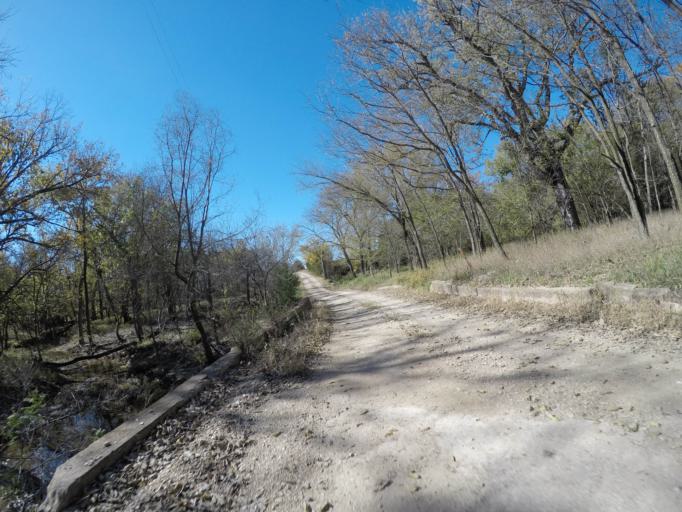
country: US
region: Kansas
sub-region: Wabaunsee County
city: Alma
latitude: 39.0290
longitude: -96.3894
